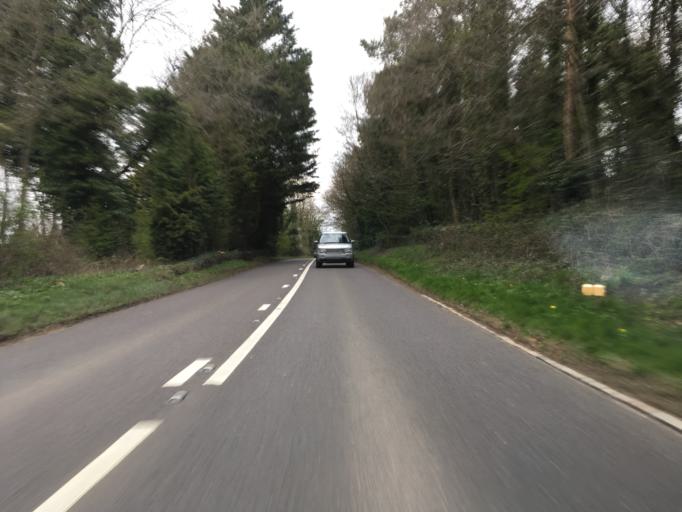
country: GB
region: England
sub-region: Gloucestershire
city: Coates
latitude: 51.6893
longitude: -2.0043
